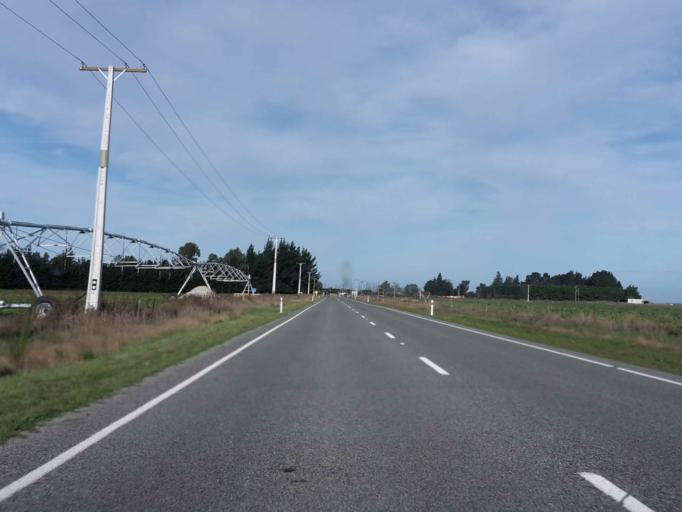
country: NZ
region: Canterbury
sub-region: Timaru District
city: Pleasant Point
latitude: -44.0639
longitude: 171.3622
